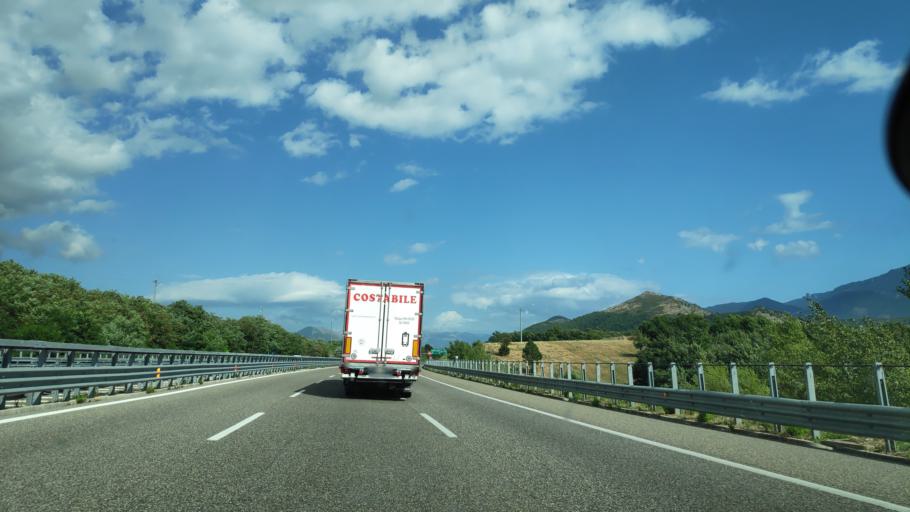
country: IT
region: Campania
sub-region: Provincia di Salerno
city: Contursi Terme
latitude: 40.6141
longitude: 15.2767
